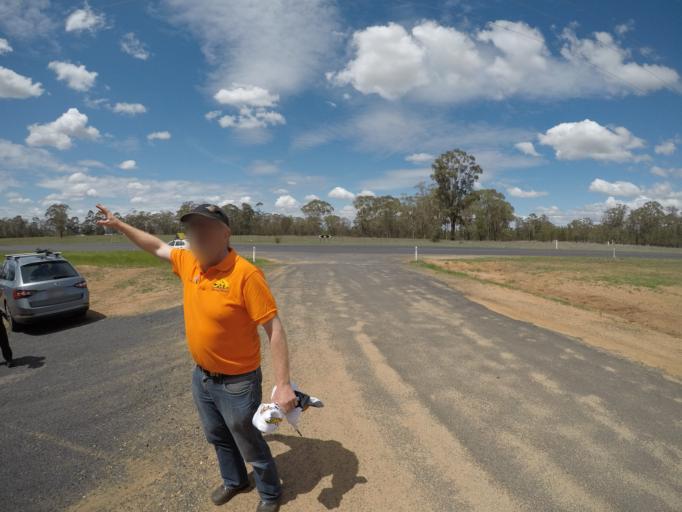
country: AU
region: New South Wales
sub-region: Dubbo Municipality
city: Dubbo
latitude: -32.3064
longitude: 148.5930
